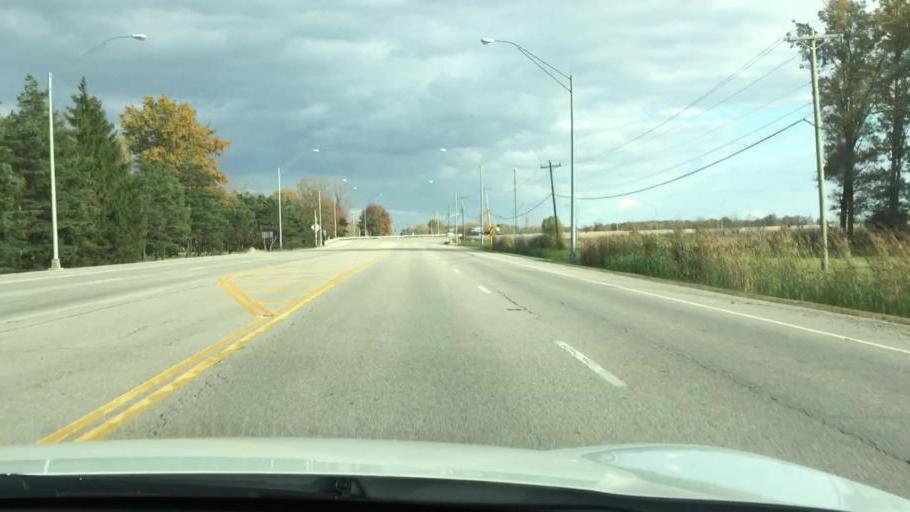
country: US
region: Ohio
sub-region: Champaign County
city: North Lewisburg
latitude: 40.2724
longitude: -83.5004
